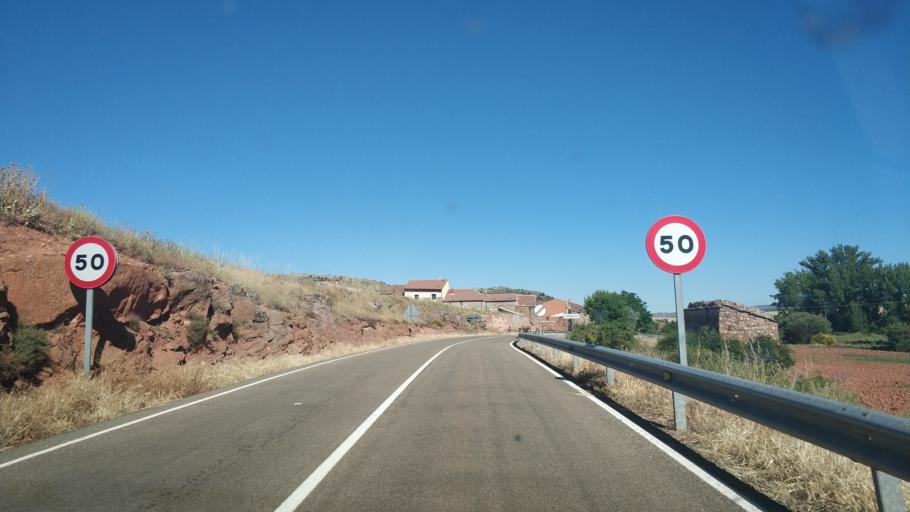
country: ES
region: Castille and Leon
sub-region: Provincia de Soria
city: Montejo de Tiermes
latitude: 41.3625
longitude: -3.1851
